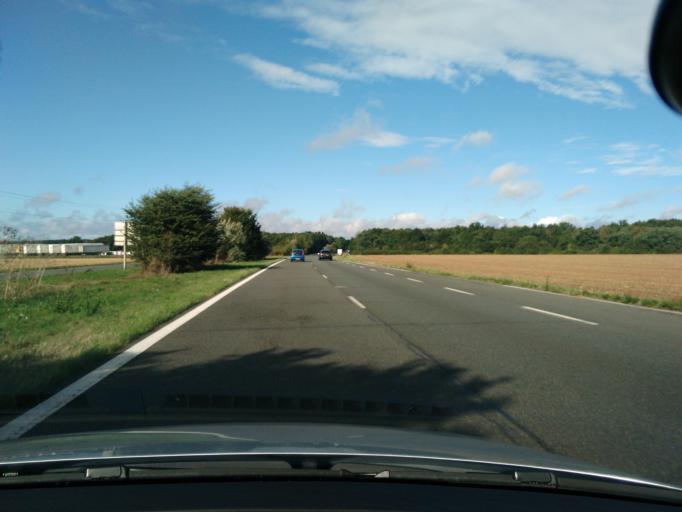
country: FR
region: Haute-Normandie
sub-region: Departement de l'Eure
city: Saint-Germain-sur-Avre
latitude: 48.7496
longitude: 1.2659
